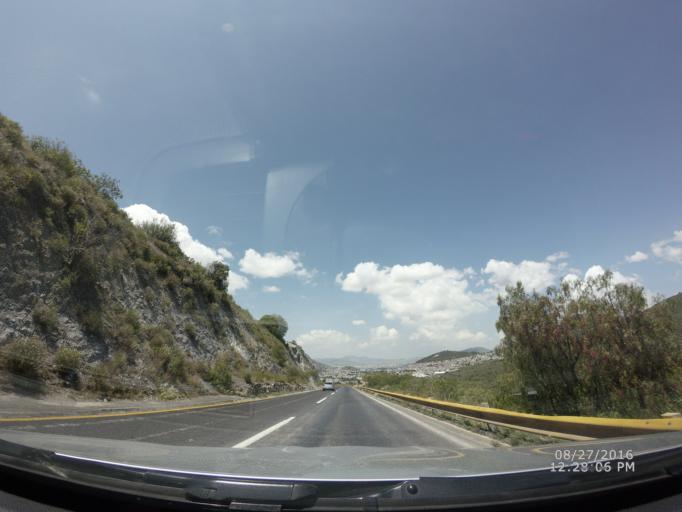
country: MX
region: Hidalgo
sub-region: Mineral de la Reforma
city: Colonia Militar
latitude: 20.1210
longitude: -98.7007
